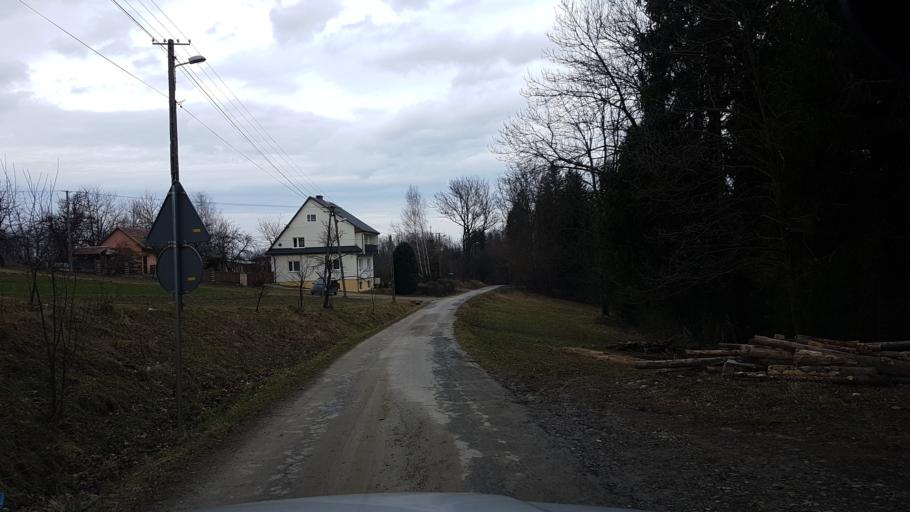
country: PL
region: Lesser Poland Voivodeship
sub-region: Powiat nowosadecki
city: Stary Sacz
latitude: 49.5328
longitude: 20.6321
